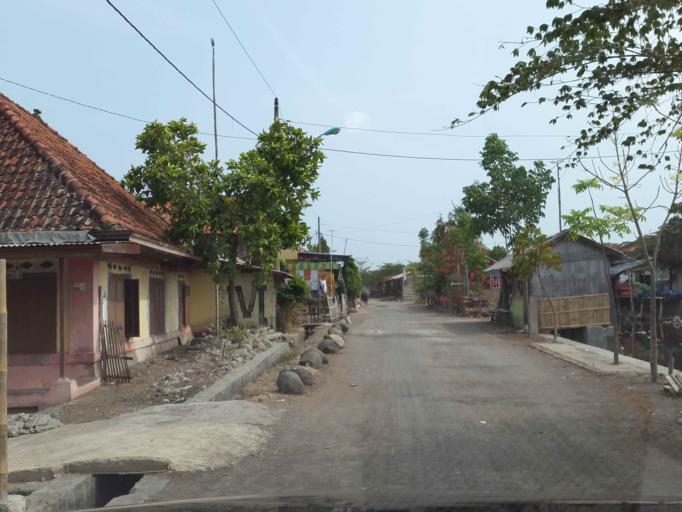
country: ID
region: Central Java
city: Bulakamba
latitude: -6.8521
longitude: 108.8842
